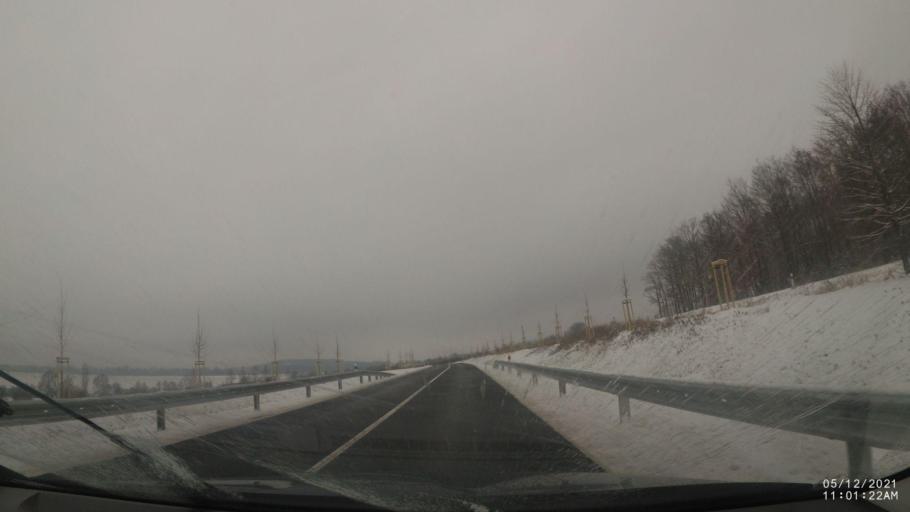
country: CZ
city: Solnice
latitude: 50.1724
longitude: 16.2220
